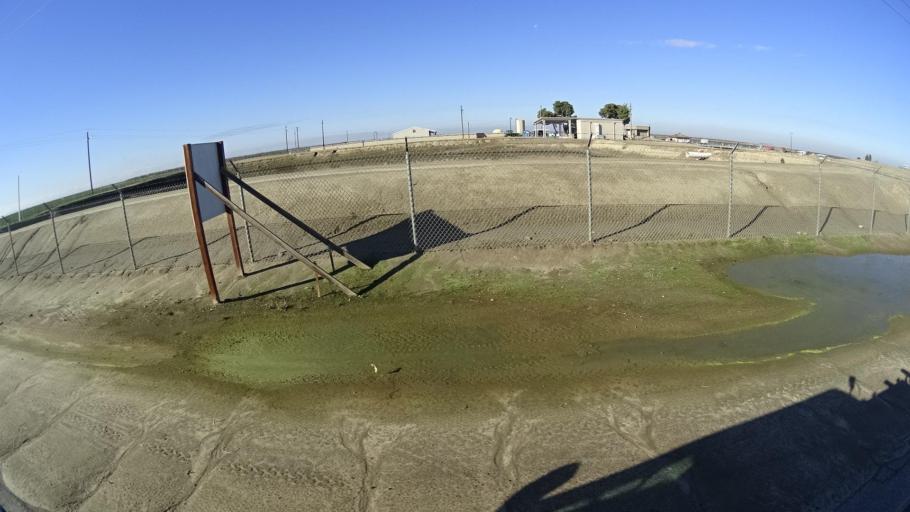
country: US
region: California
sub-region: Kern County
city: McFarland
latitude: 35.6822
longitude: -119.2764
